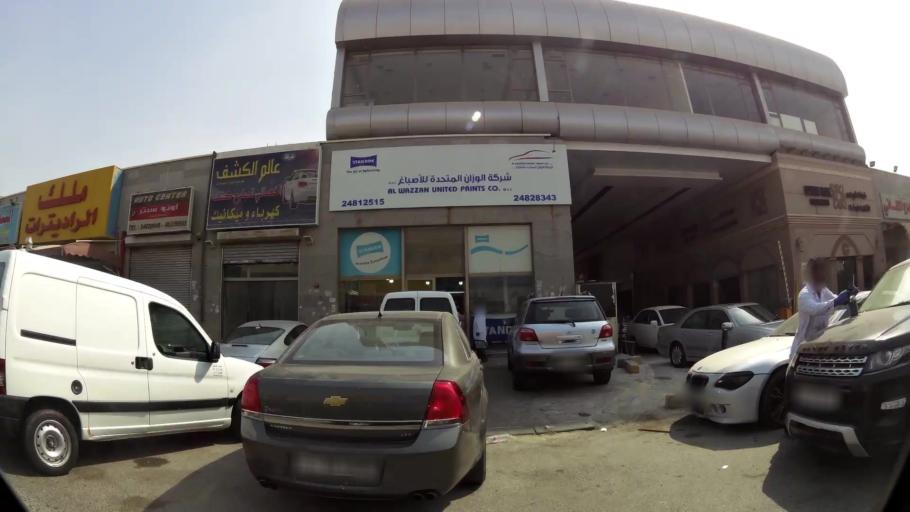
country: KW
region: Al Asimah
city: Ash Shamiyah
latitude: 29.3285
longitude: 47.9407
